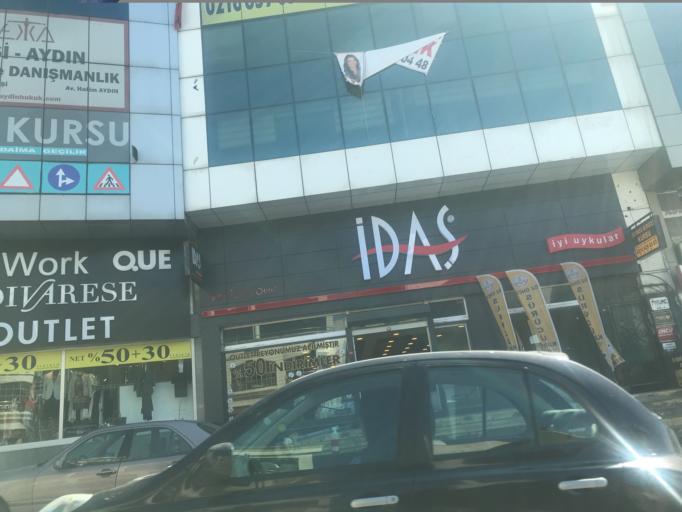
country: TR
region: Istanbul
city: Umraniye
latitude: 41.0317
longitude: 29.1732
